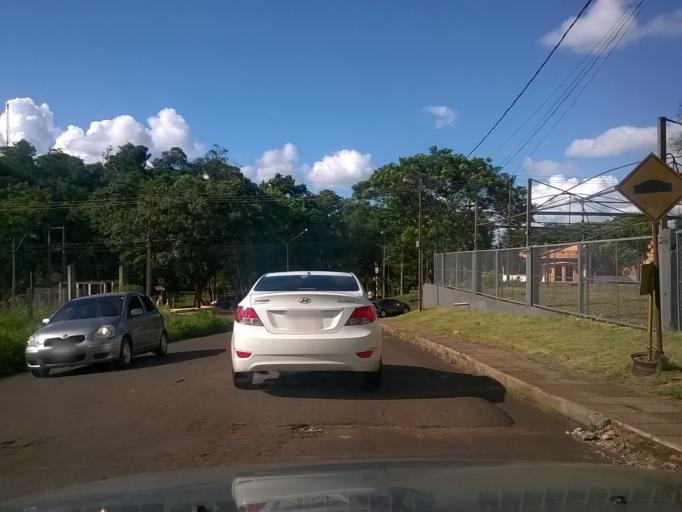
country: PY
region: Alto Parana
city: Presidente Franco
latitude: -25.5253
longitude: -54.6260
